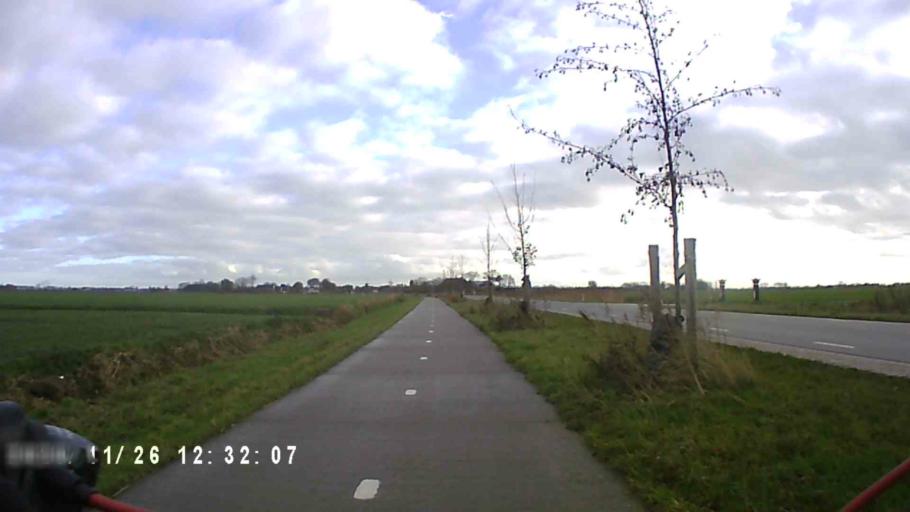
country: NL
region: Groningen
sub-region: Gemeente Bedum
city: Bedum
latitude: 53.3267
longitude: 6.7223
